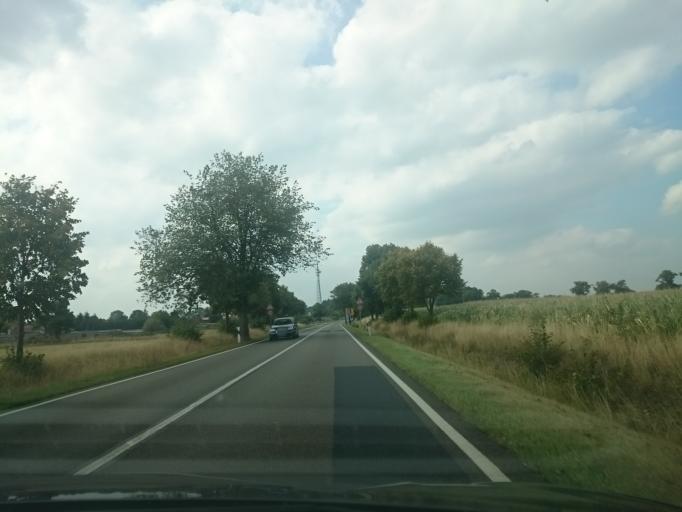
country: DE
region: Mecklenburg-Vorpommern
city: Ferdinandshof
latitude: 53.6662
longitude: 13.8941
